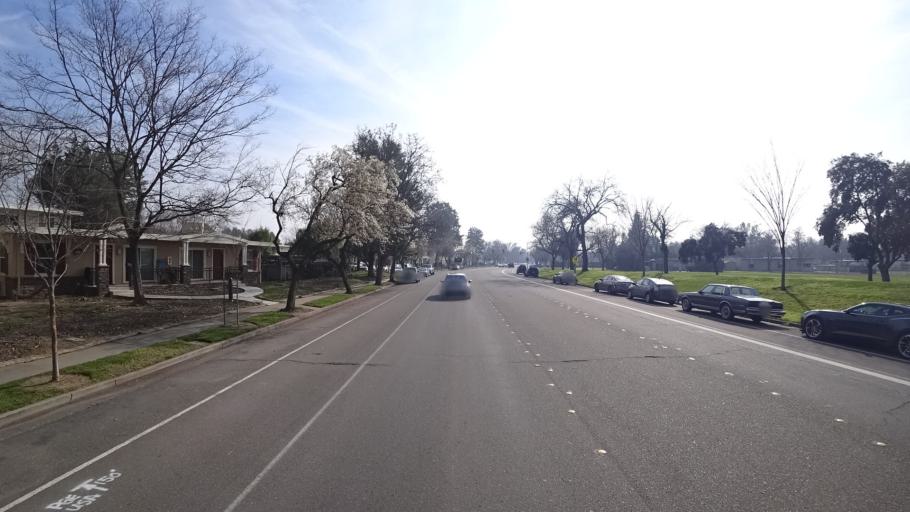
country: US
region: California
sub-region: Yolo County
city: Davis
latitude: 38.5583
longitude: -121.7440
